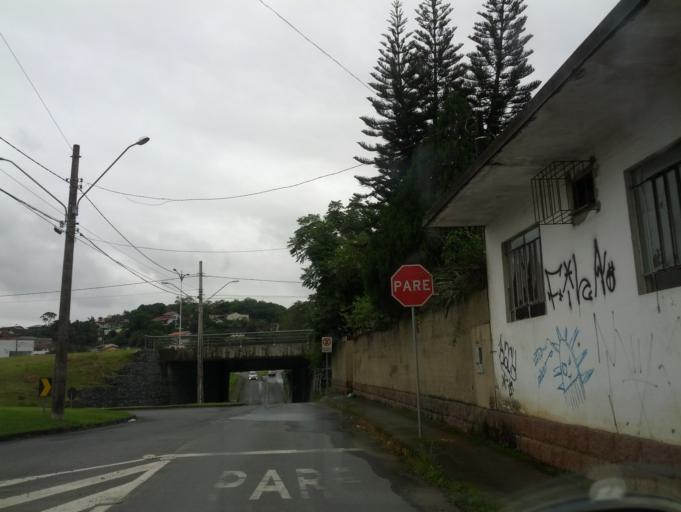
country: BR
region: Santa Catarina
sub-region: Blumenau
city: Blumenau
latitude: -26.8889
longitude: -49.0691
